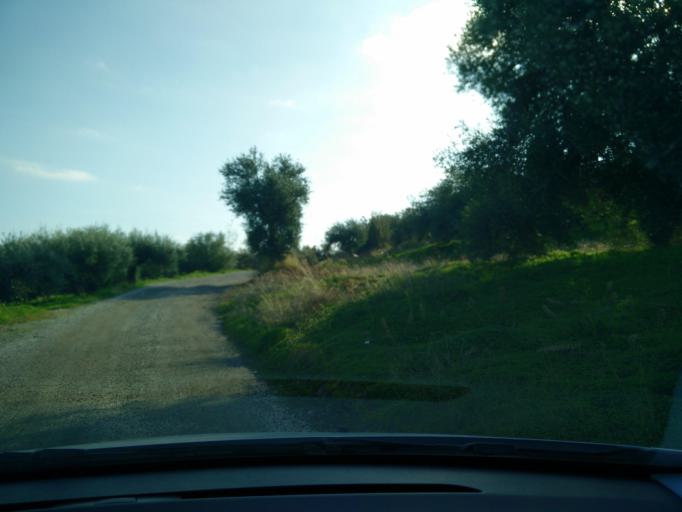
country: GR
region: Crete
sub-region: Nomos Lasithiou
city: Gra Liyia
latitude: 35.0298
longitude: 25.5669
